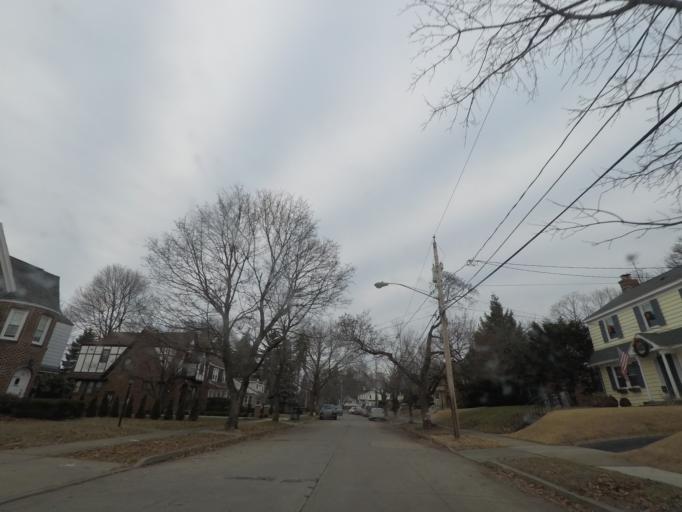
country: US
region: New York
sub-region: Albany County
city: Green Island
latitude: 42.7395
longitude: -73.6659
